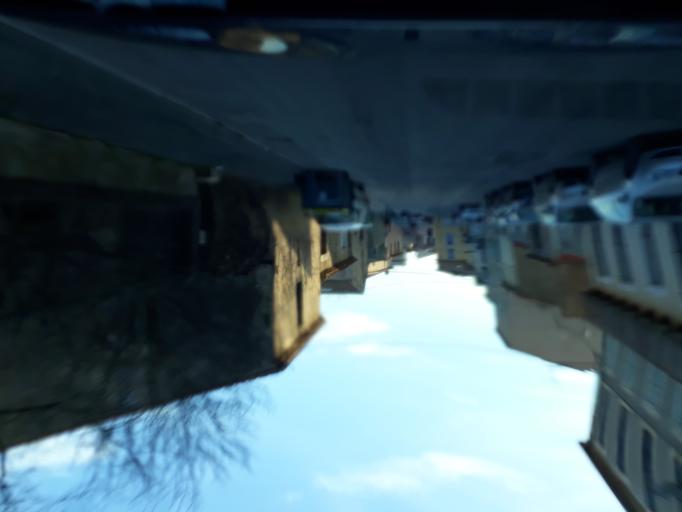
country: FR
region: Languedoc-Roussillon
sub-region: Departement de l'Herault
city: Marseillan
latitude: 43.3550
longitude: 3.5312
